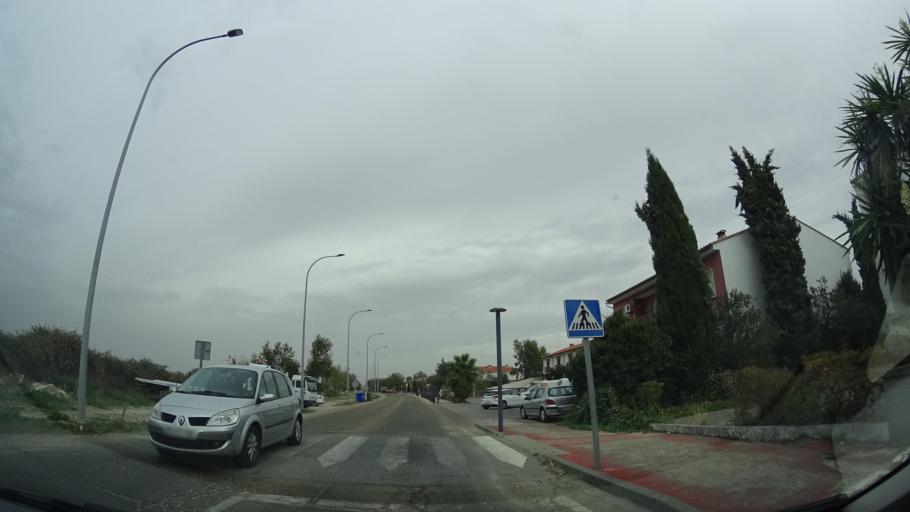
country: ES
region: Extremadura
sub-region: Provincia de Caceres
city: Trujillo
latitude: 39.4611
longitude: -5.8696
